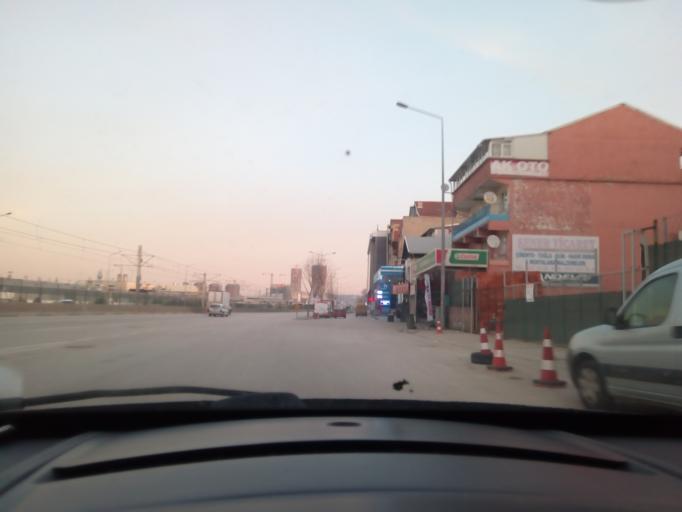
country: TR
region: Bursa
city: Niluefer
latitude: 40.2542
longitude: 28.9542
